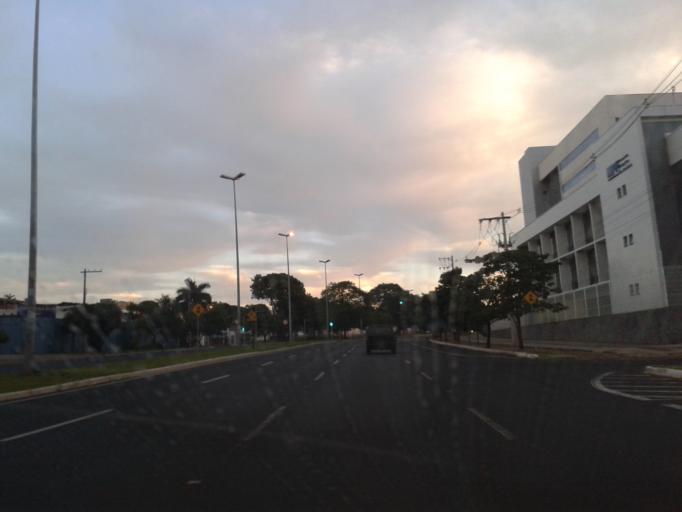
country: BR
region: Minas Gerais
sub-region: Uberlandia
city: Uberlandia
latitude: -18.8992
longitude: -48.2581
